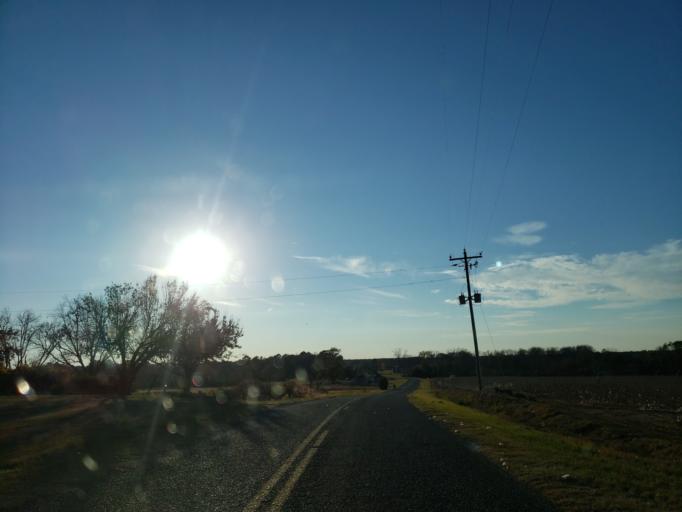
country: US
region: Georgia
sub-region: Dooly County
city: Unadilla
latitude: 32.2095
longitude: -83.7850
